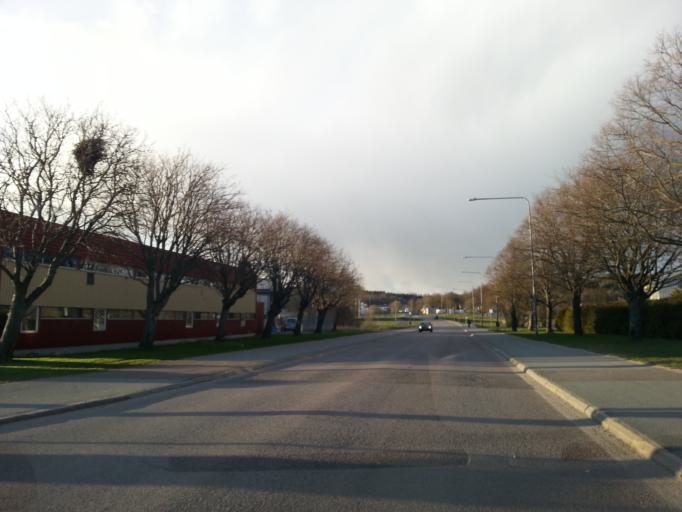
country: SE
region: Vaestra Goetaland
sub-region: Kungalvs Kommun
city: Kungalv
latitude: 57.8781
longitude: 11.9854
